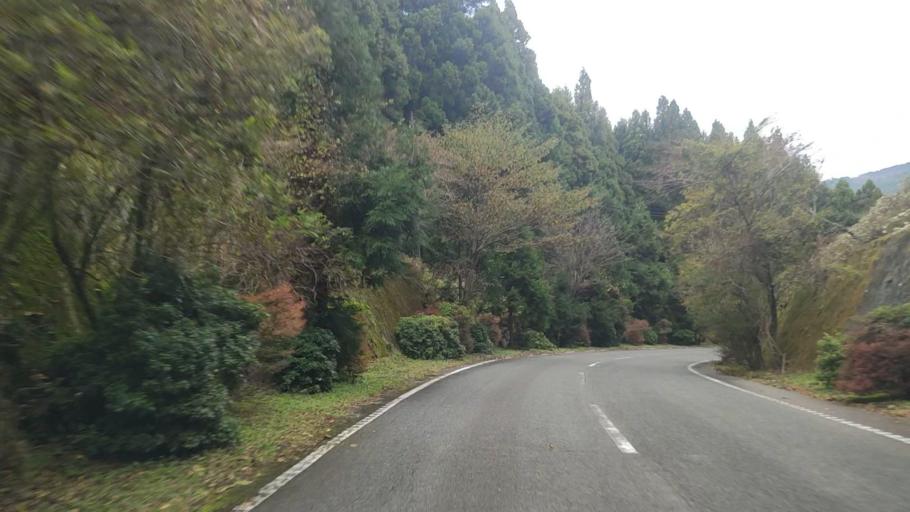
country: JP
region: Shizuoka
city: Heda
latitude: 34.9157
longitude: 138.8428
